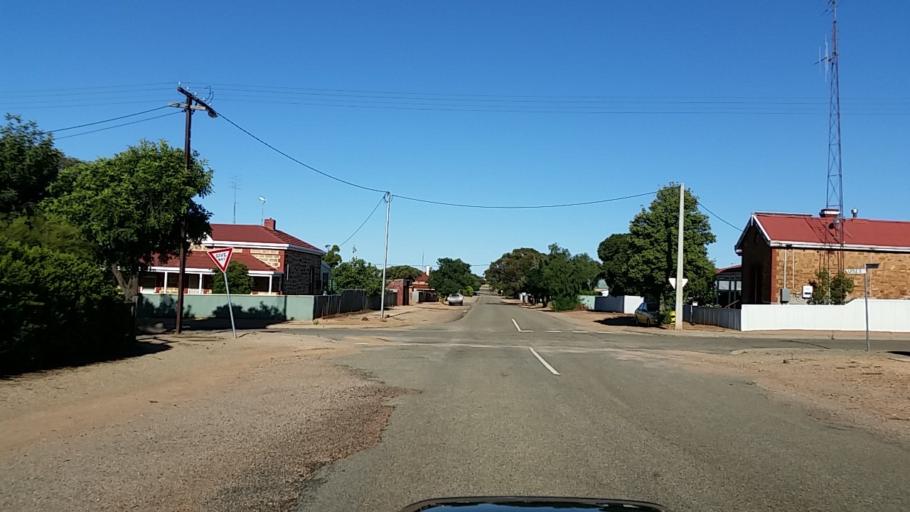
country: AU
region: South Australia
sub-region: Peterborough
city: Peterborough
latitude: -32.9759
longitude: 138.8356
